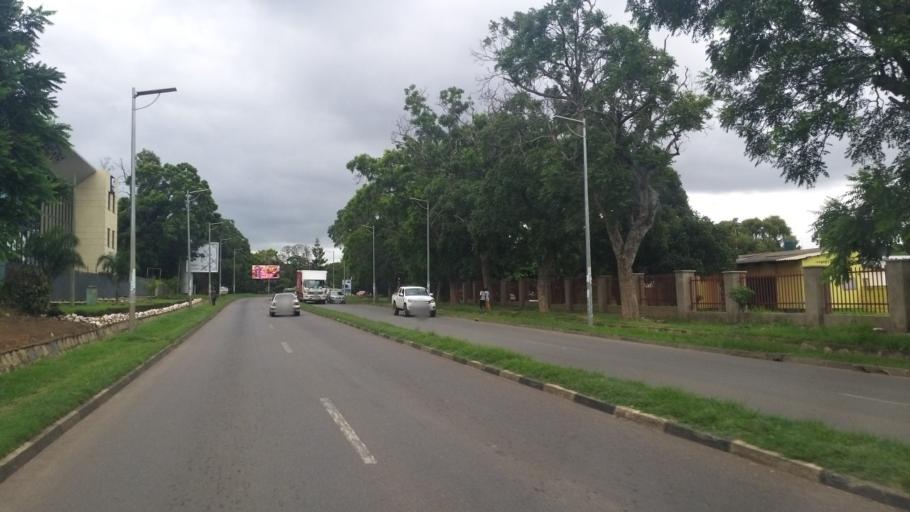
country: ZM
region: Lusaka
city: Lusaka
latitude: -15.4196
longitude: 28.3164
